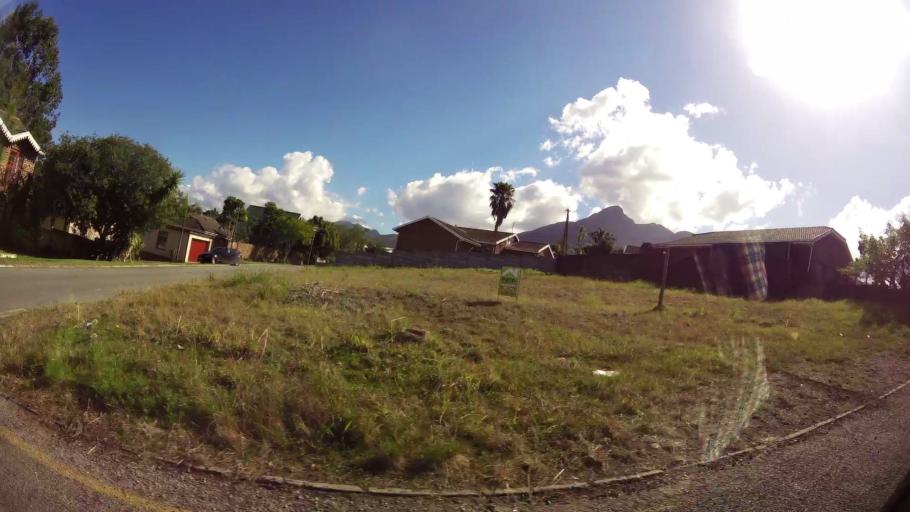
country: ZA
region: Western Cape
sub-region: Eden District Municipality
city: George
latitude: -33.9497
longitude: 22.4797
